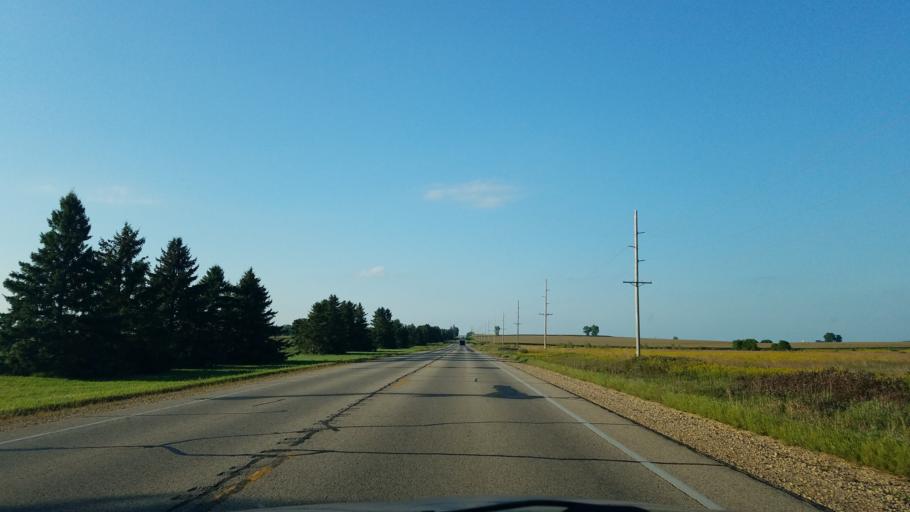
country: US
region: Wisconsin
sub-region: Saint Croix County
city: Roberts
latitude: 45.0107
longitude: -92.5377
